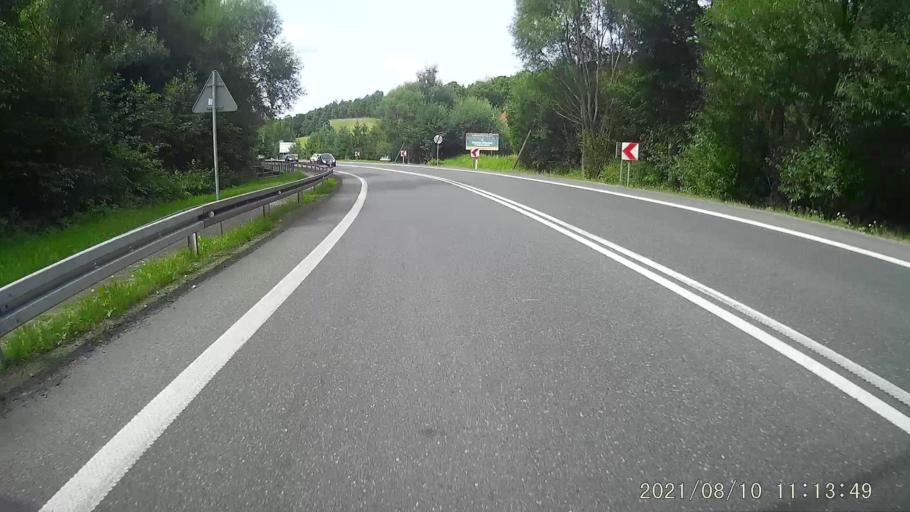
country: PL
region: Lower Silesian Voivodeship
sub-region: Powiat klodzki
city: Szczytna
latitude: 50.4115
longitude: 16.4218
